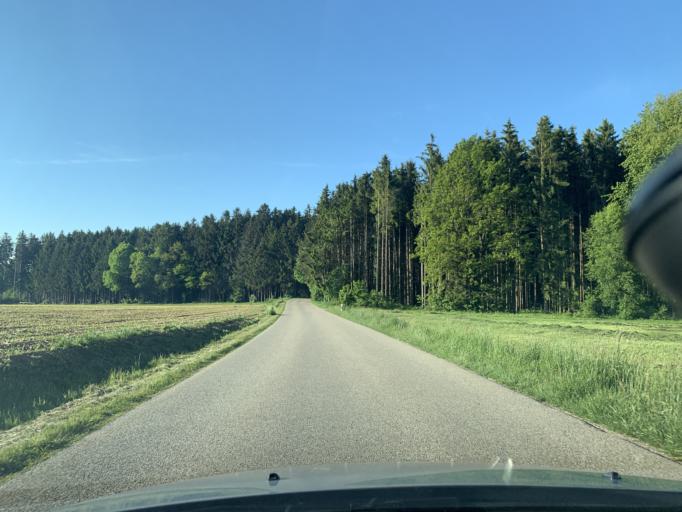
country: DE
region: Bavaria
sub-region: Lower Bavaria
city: Vilsbiburg
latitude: 48.4880
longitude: 12.3760
